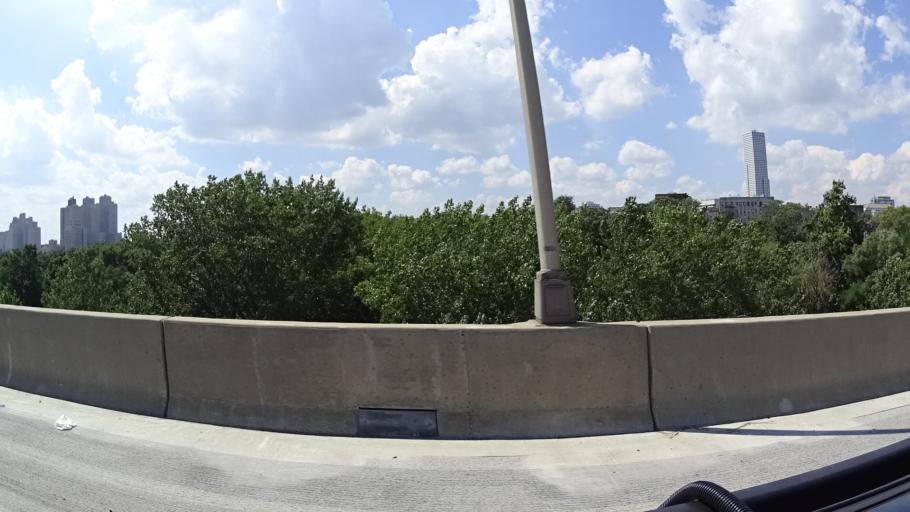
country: US
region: New Jersey
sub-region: Hudson County
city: Jersey City
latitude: 40.7264
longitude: -74.0533
